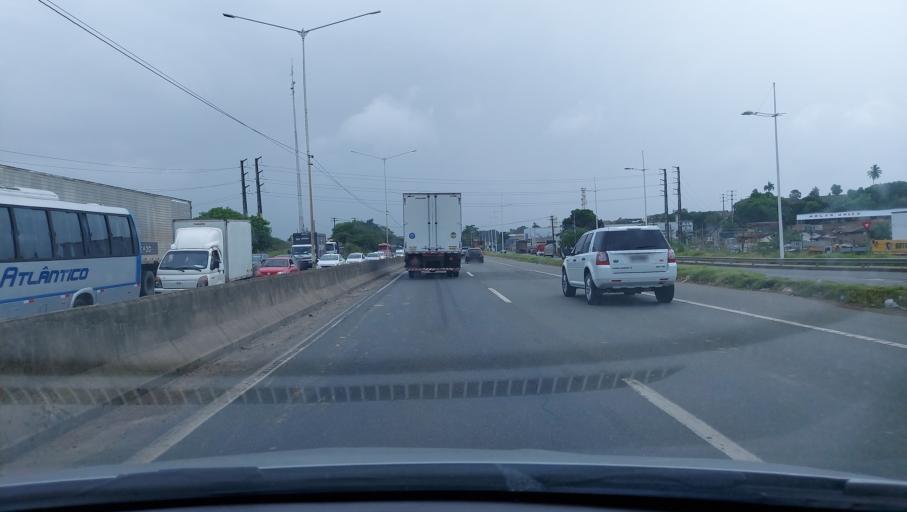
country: BR
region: Bahia
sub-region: Salvador
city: Salvador
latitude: -12.8891
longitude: -38.4428
